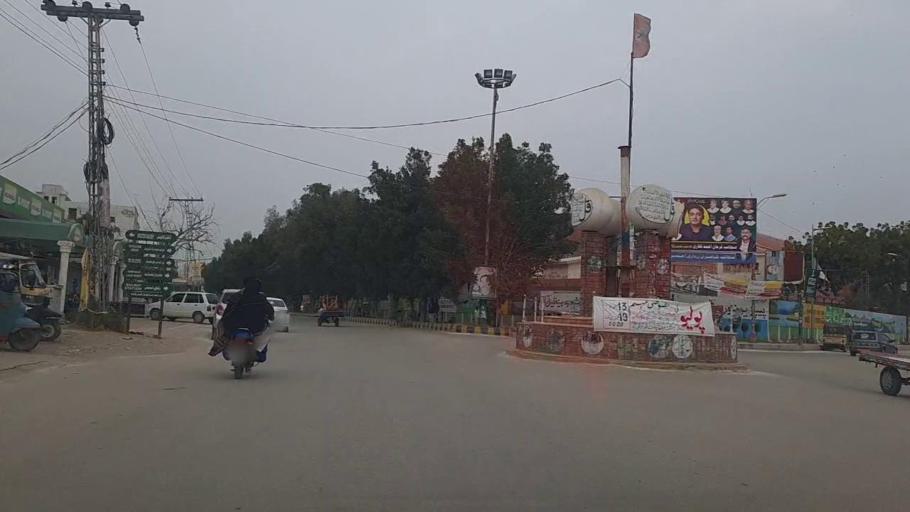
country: PK
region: Sindh
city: Nawabshah
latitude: 26.2418
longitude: 68.4014
